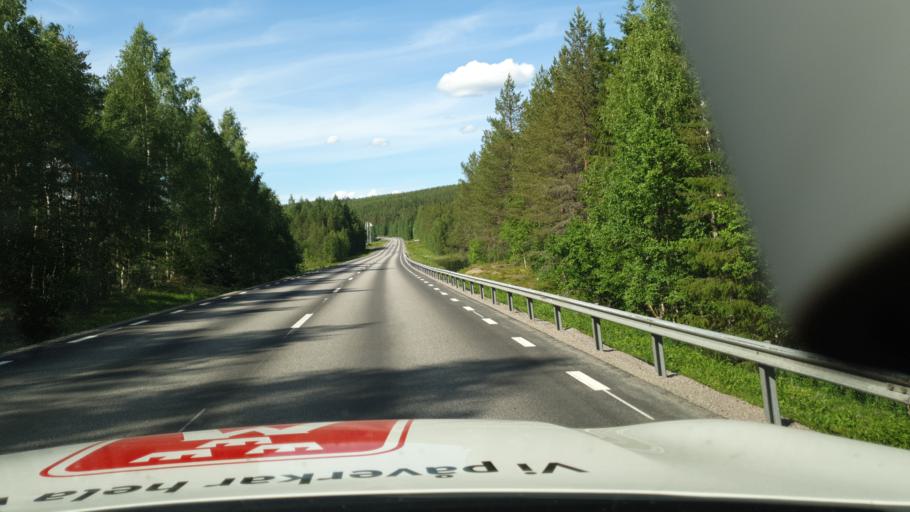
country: SE
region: Vaesterbotten
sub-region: Skelleftea Kommun
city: Boliden
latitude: 64.8923
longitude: 20.3756
